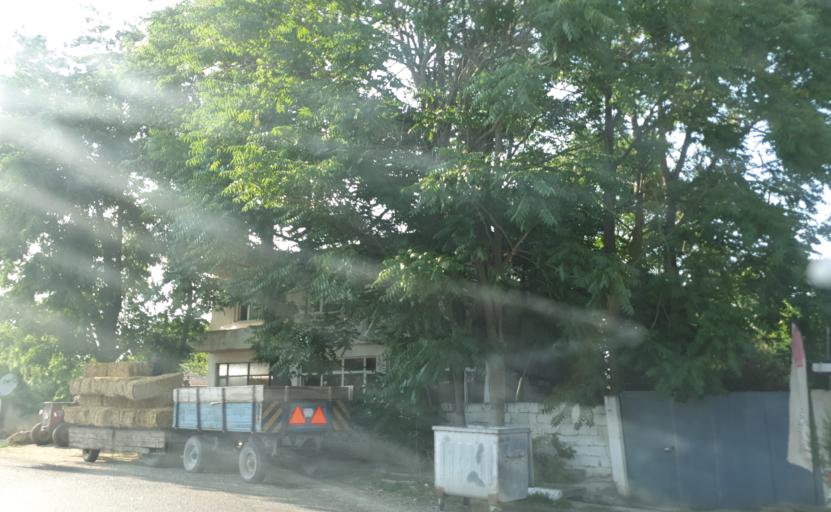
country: TR
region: Tekirdag
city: Muratli
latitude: 41.2020
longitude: 27.4714
